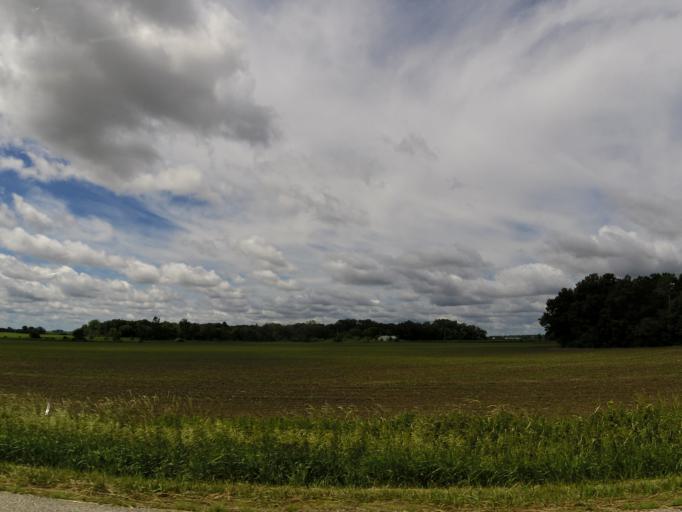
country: US
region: Minnesota
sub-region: Fillmore County
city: Spring Valley
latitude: 43.7065
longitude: -92.4155
